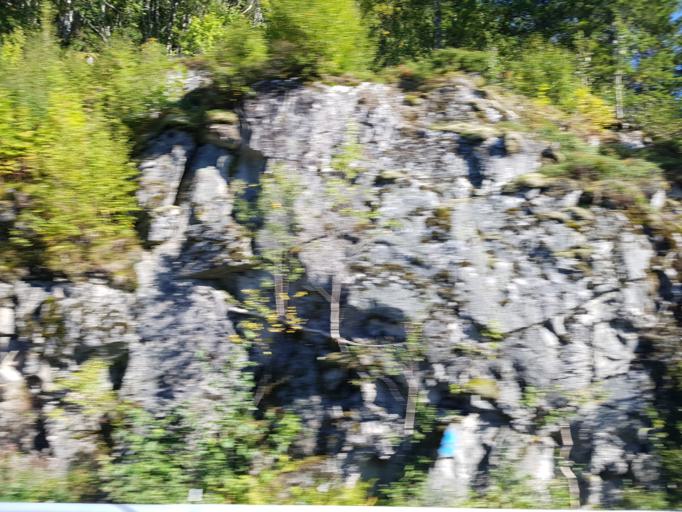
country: NO
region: Sor-Trondelag
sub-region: Afjord
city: A i Afjord
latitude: 63.7598
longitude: 10.2398
